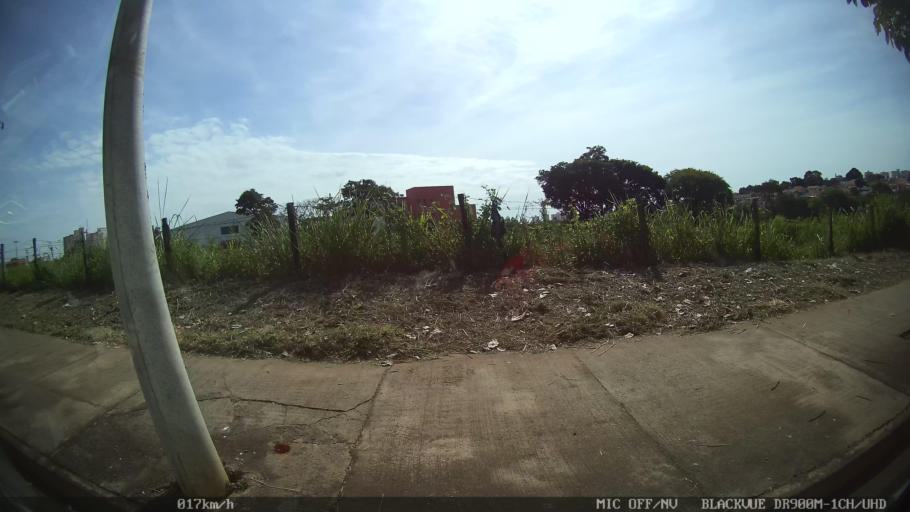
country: BR
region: Sao Paulo
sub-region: Piracicaba
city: Piracicaba
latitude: -22.7465
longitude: -47.6278
